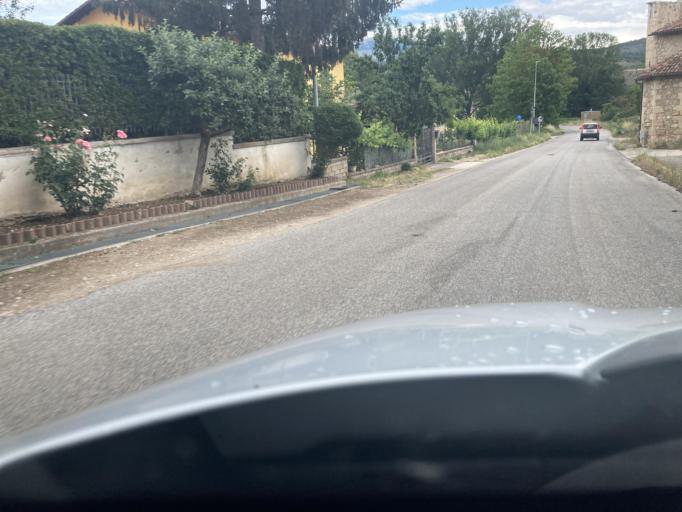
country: IT
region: Abruzzo
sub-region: Provincia dell' Aquila
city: Sant'Eusanio Forconese
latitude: 42.2921
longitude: 13.5273
